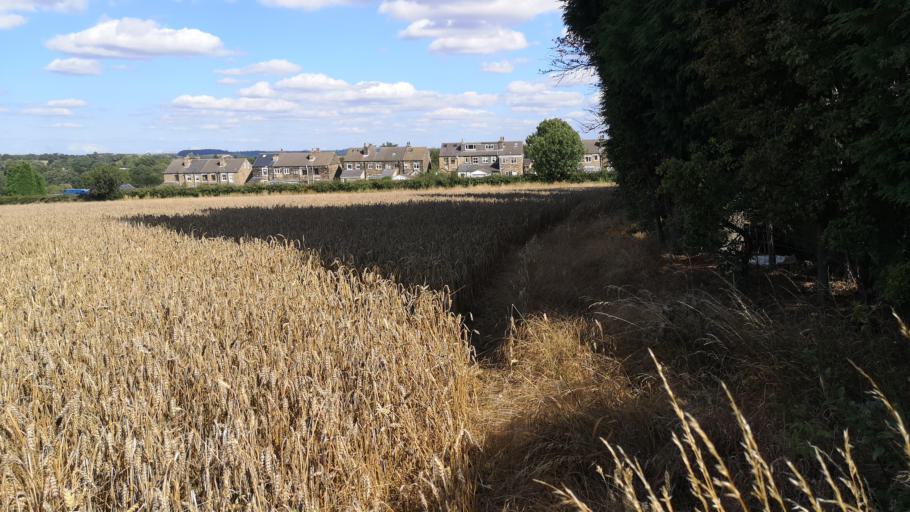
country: GB
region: England
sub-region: City and Borough of Wakefield
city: Low Ackworth
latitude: 53.6457
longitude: -1.3491
